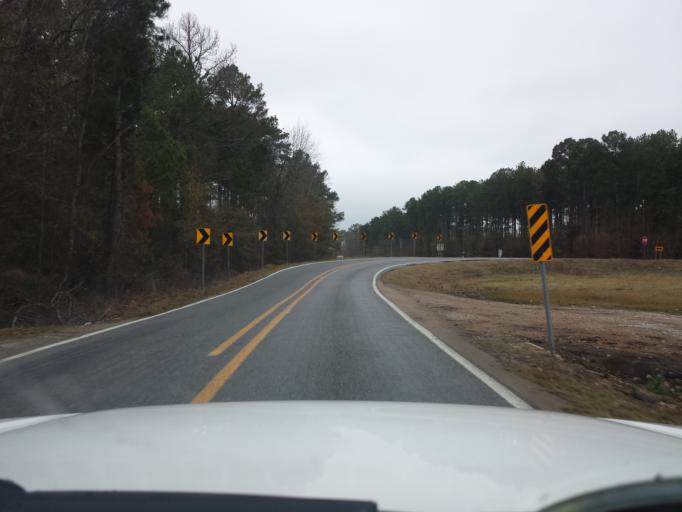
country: US
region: Mississippi
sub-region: Madison County
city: Canton
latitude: 32.4984
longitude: -89.9257
